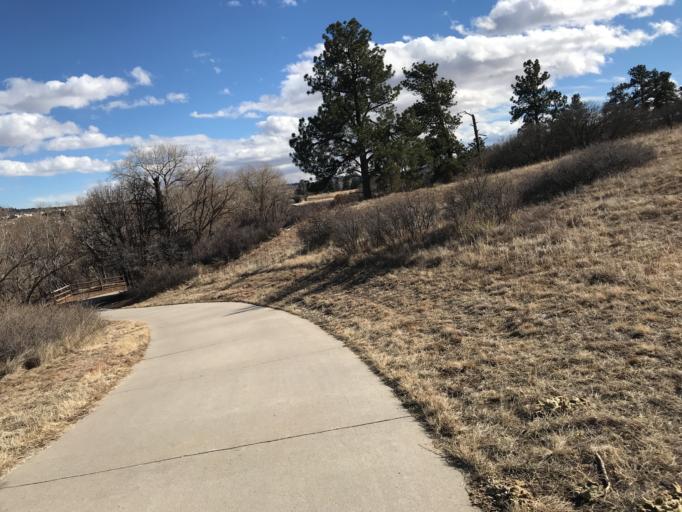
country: US
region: Colorado
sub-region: Douglas County
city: Castle Rock
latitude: 39.4101
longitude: -104.8836
